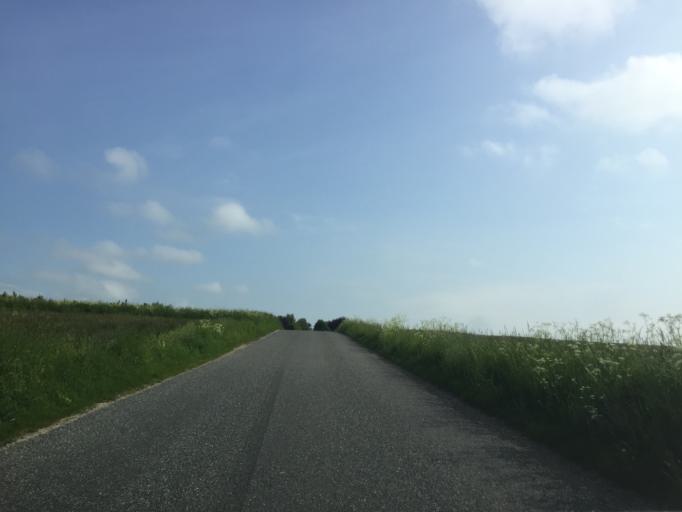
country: DK
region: South Denmark
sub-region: Svendborg Kommune
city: Thuro By
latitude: 55.1222
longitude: 10.7440
